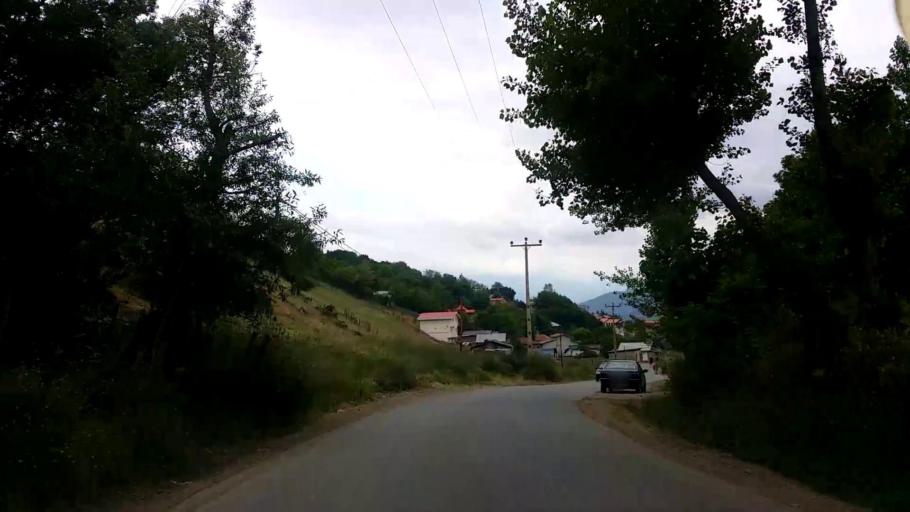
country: IR
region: Mazandaran
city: Chalus
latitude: 36.5186
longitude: 51.2598
